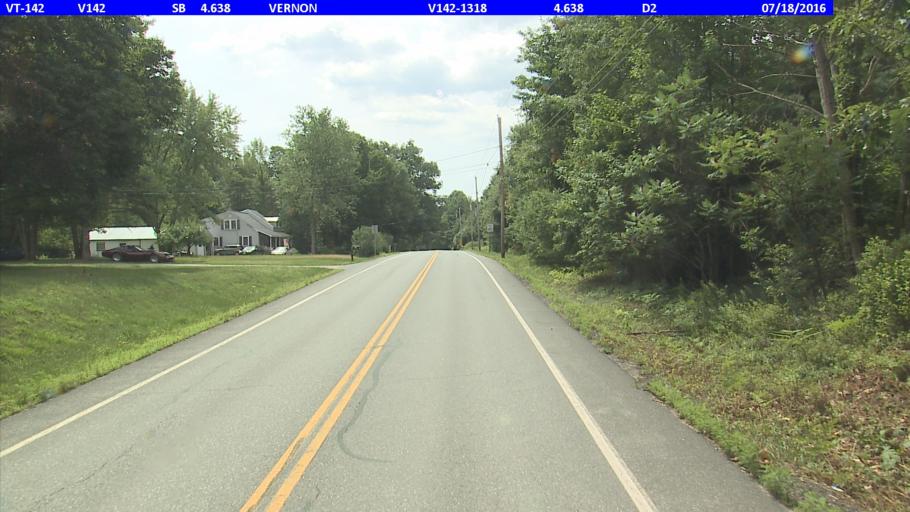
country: US
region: New Hampshire
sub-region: Cheshire County
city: Hinsdale
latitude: 42.7716
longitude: -72.5202
